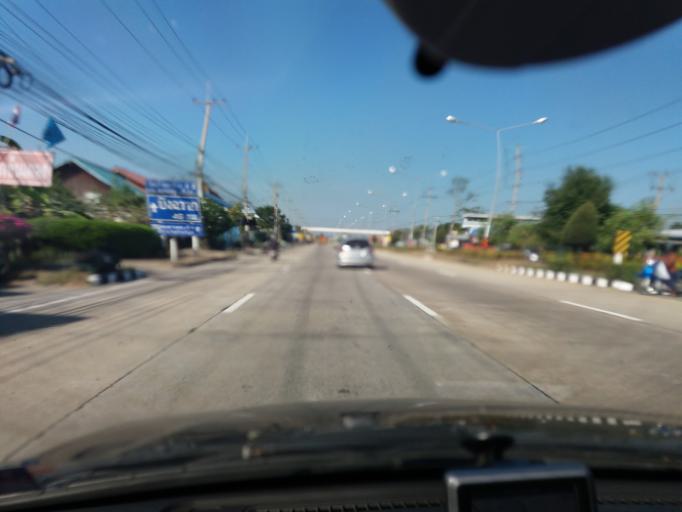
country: TH
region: Suphan Buri
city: Si Prachan
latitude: 14.6017
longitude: 100.1556
